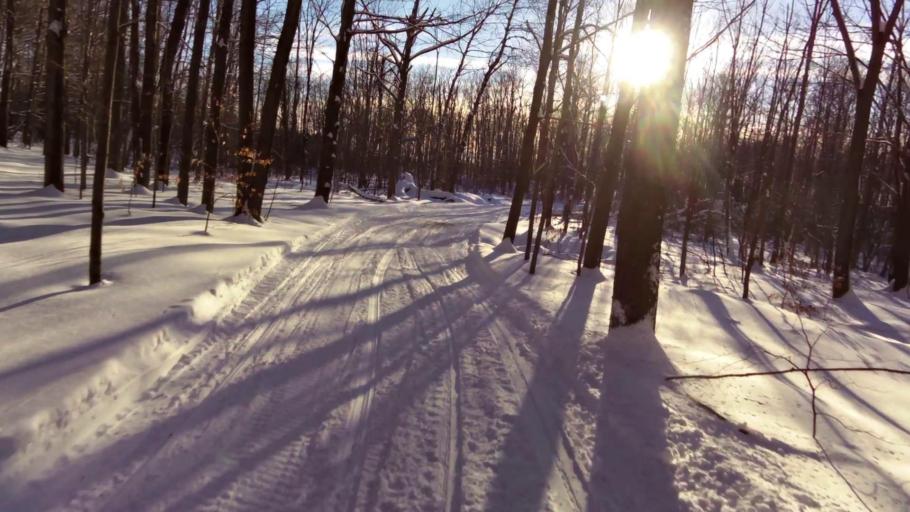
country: US
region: New York
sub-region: Chautauqua County
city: Mayville
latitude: 42.2461
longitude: -79.3926
